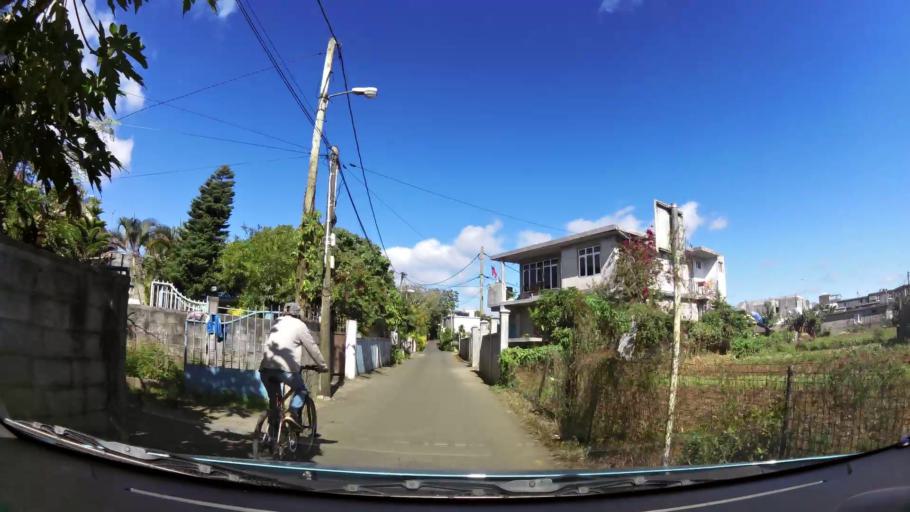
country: MU
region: Plaines Wilhems
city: Vacoas
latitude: -20.3176
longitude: 57.4871
